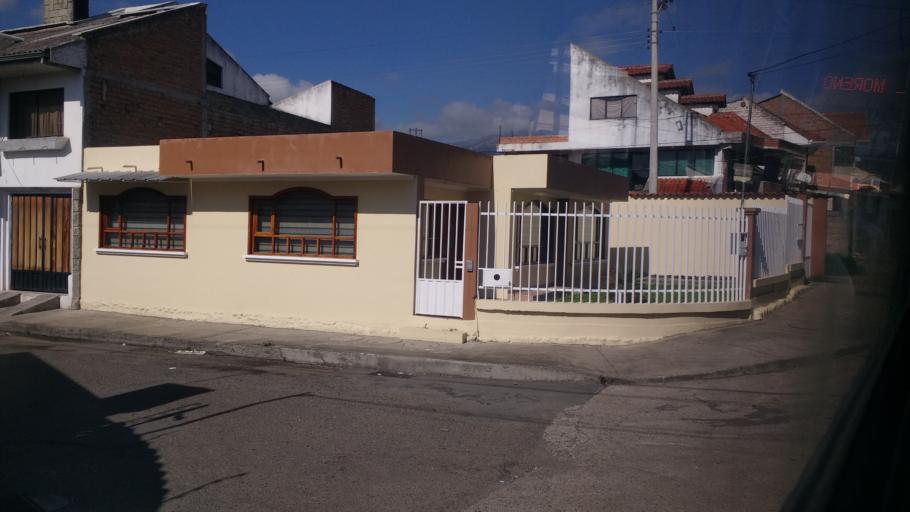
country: EC
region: Azuay
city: Cuenca
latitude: -2.9012
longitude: -79.0313
